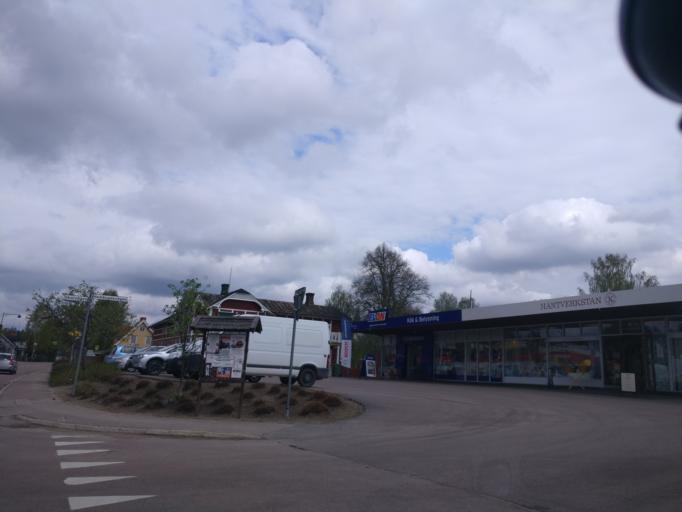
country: SE
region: Vaermland
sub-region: Hagfors Kommun
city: Ekshaerad
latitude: 60.1755
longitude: 13.4958
